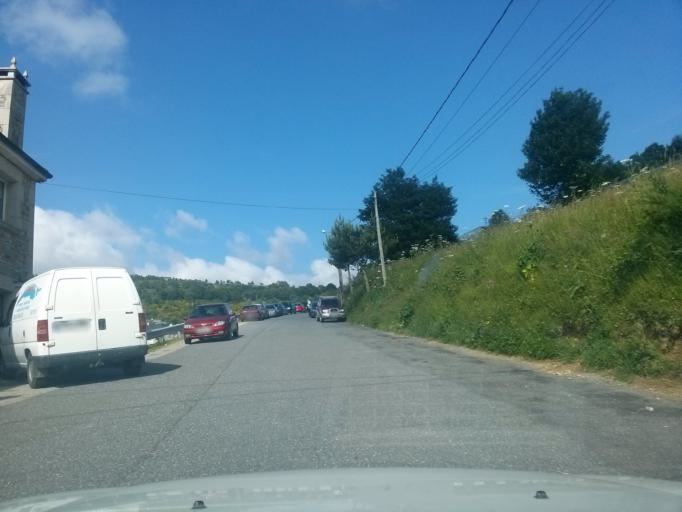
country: ES
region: Castille and Leon
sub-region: Provincia de Leon
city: Balboa
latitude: 42.7256
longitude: -7.0233
